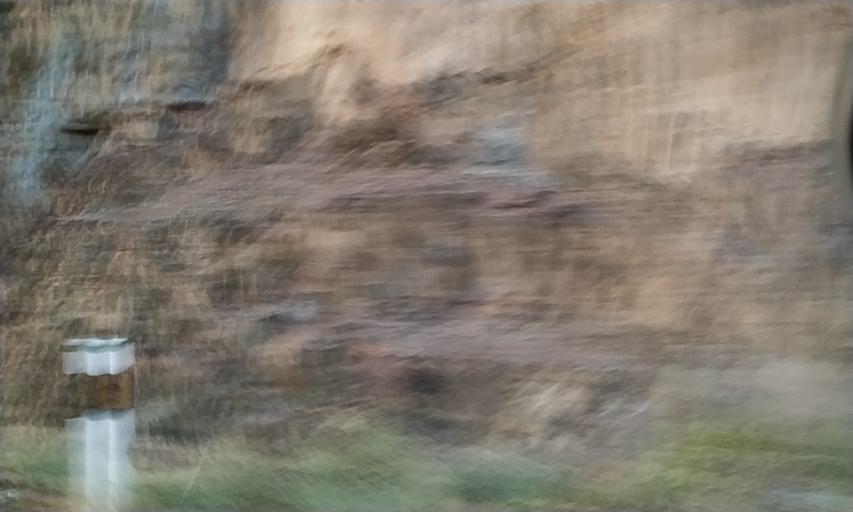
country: ES
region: Extremadura
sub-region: Provincia de Caceres
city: Alcantara
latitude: 39.7215
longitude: -6.8805
